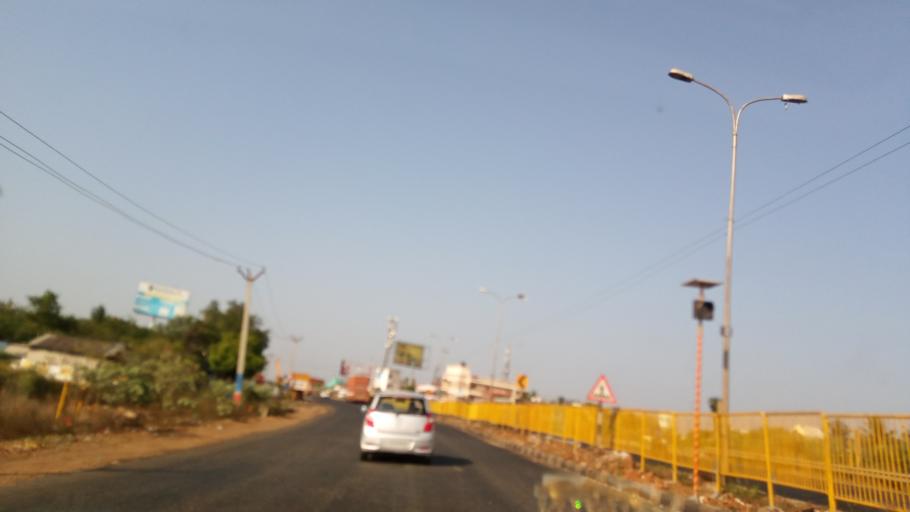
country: IN
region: Tamil Nadu
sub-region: Kancheepuram
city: Sriperumbudur
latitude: 12.9935
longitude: 79.9872
